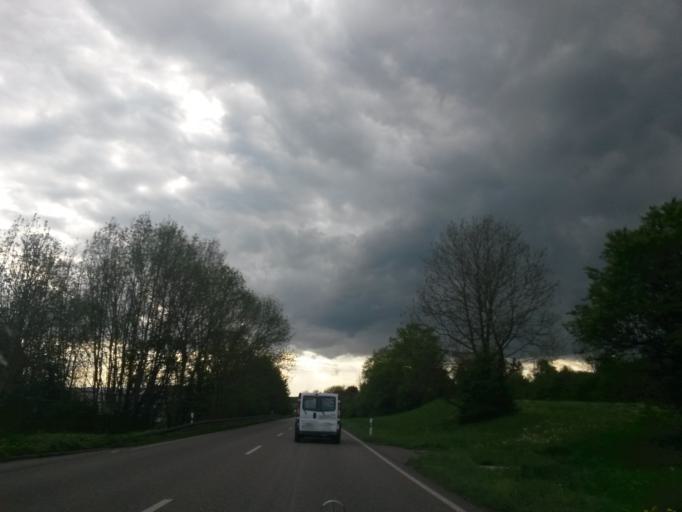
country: DE
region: Baden-Wuerttemberg
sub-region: Regierungsbezirk Stuttgart
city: Mogglingen
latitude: 48.8224
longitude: 9.9796
